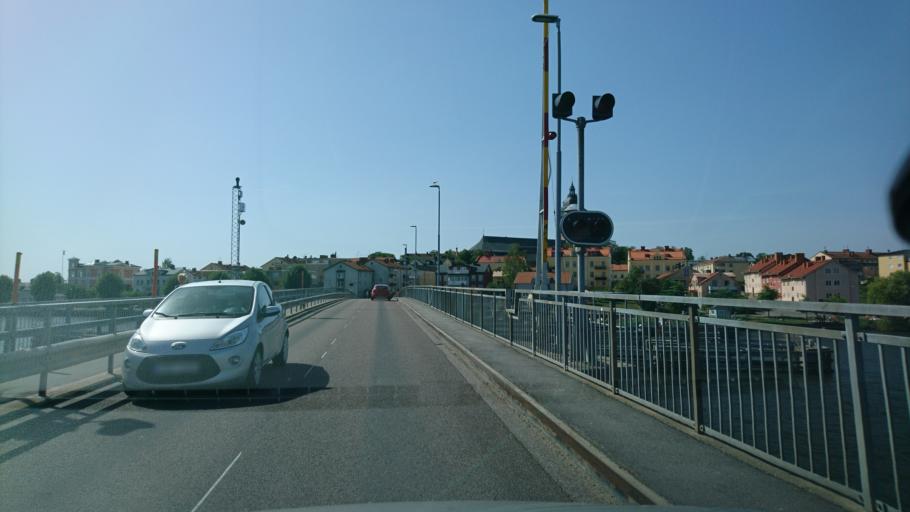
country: SE
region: Soedermanland
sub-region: Strangnas Kommun
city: Strangnas
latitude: 59.3788
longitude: 17.0383
